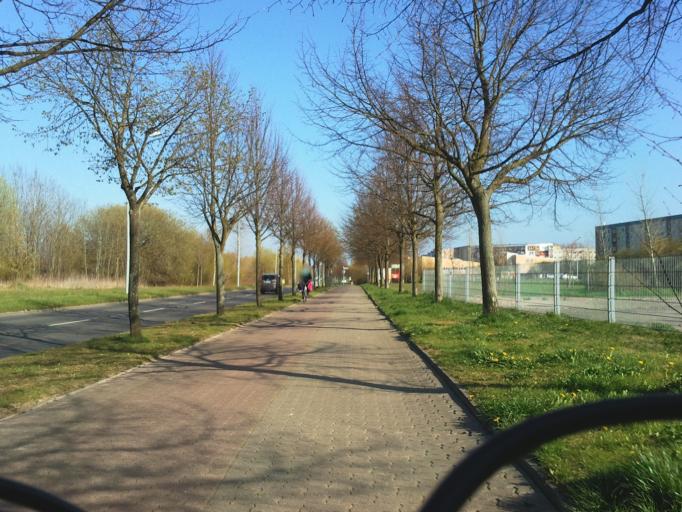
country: DE
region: Mecklenburg-Vorpommern
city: Dierkow-West
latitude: 54.1183
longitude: 12.1454
